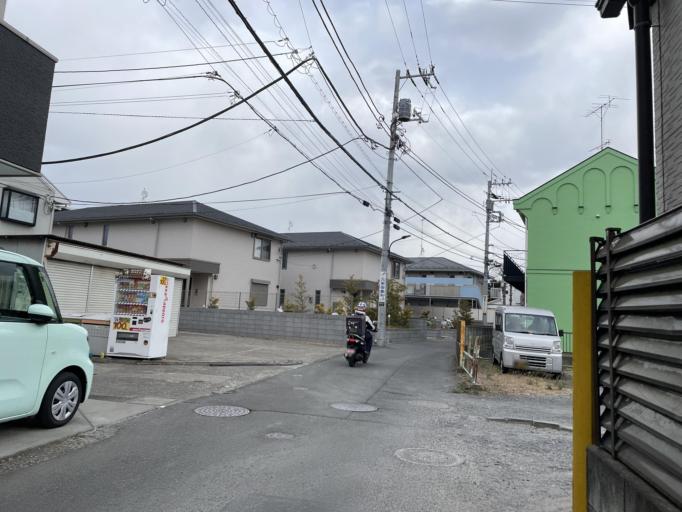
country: JP
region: Tokyo
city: Chofugaoka
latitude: 35.6330
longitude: 139.5913
